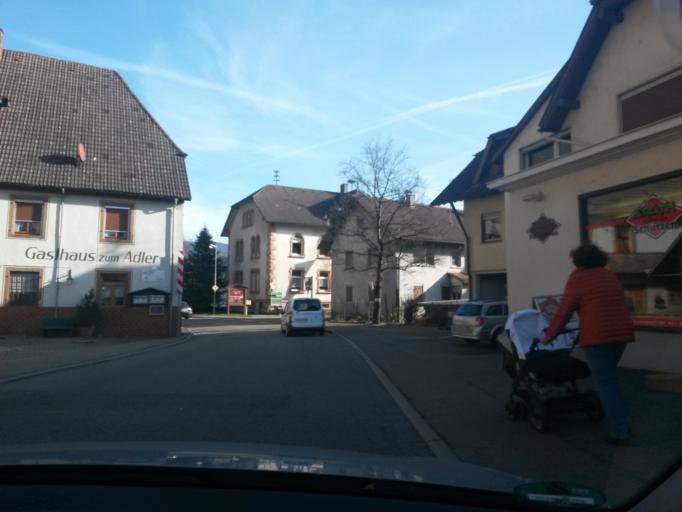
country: DE
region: Baden-Wuerttemberg
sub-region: Freiburg Region
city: Elzach
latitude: 48.1541
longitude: 8.0424
